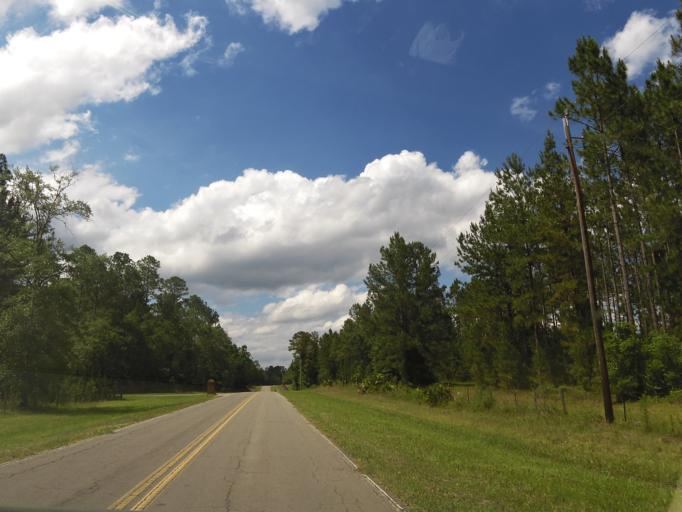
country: US
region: Florida
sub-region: Clay County
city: Asbury Lake
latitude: 29.9005
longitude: -81.8765
